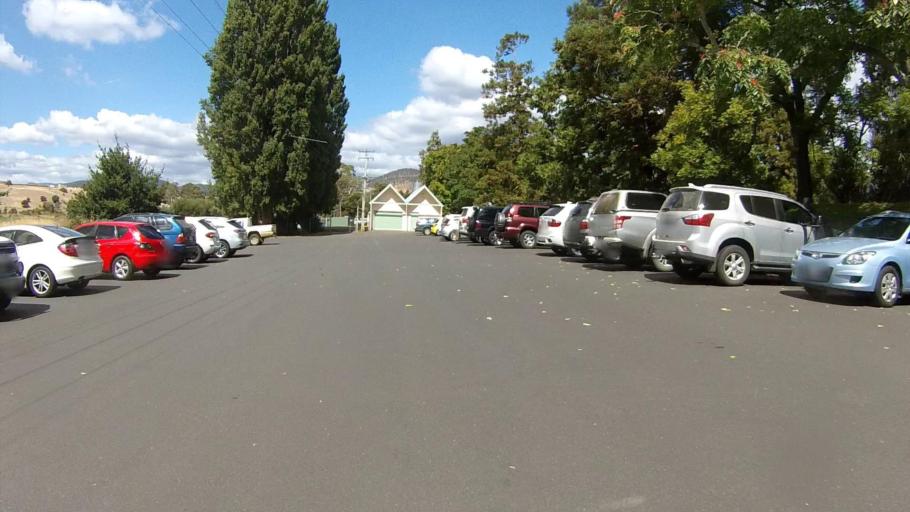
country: AU
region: Tasmania
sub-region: Derwent Valley
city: New Norfolk
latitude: -42.7535
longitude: 146.9699
